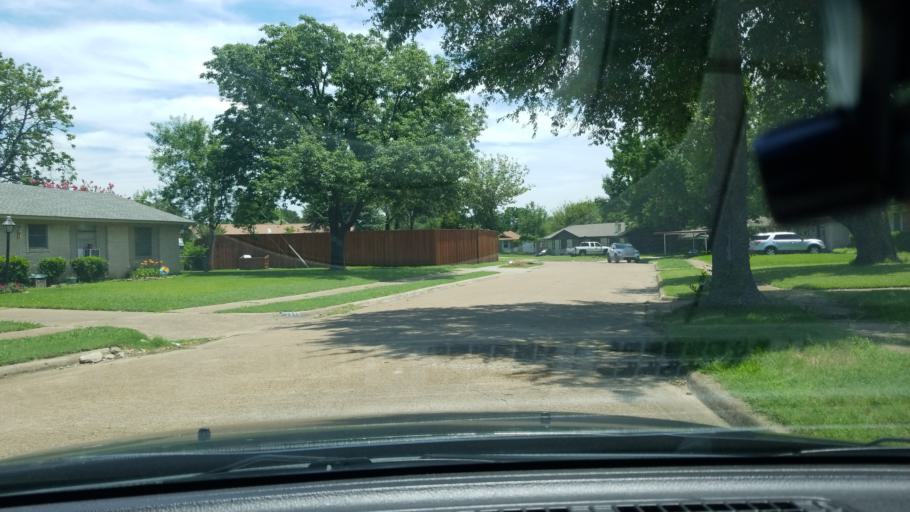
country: US
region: Texas
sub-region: Dallas County
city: Mesquite
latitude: 32.7973
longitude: -96.6579
